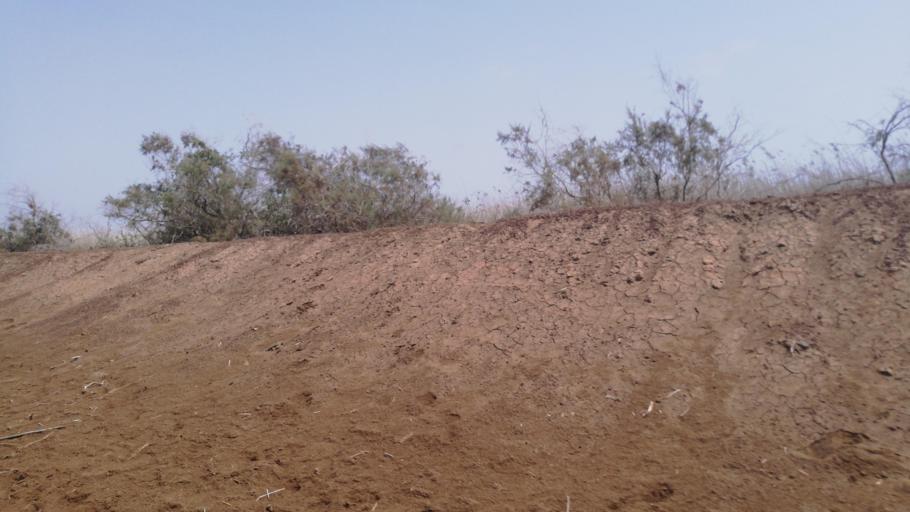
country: SN
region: Saint-Louis
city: Saint-Louis
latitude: 16.4004
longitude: -16.2897
